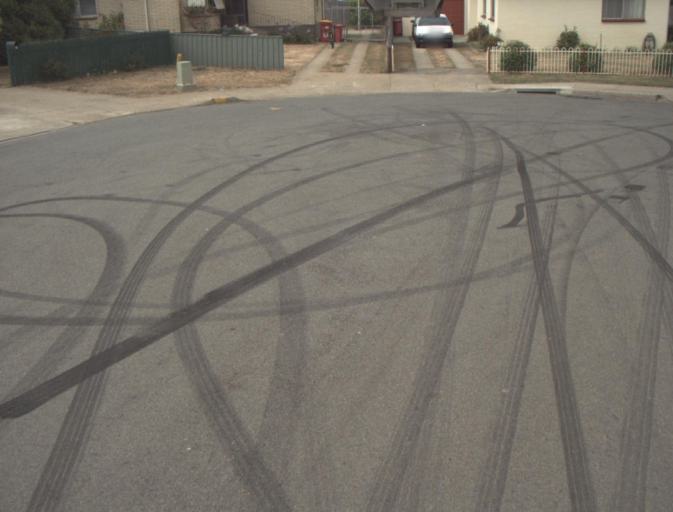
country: AU
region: Tasmania
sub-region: Launceston
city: Newstead
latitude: -41.4368
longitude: 147.1910
